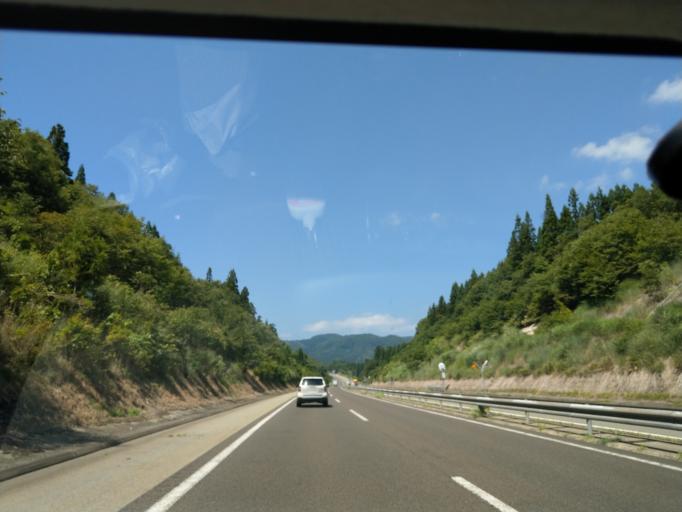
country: JP
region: Akita
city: Omagari
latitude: 39.4147
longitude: 140.4378
